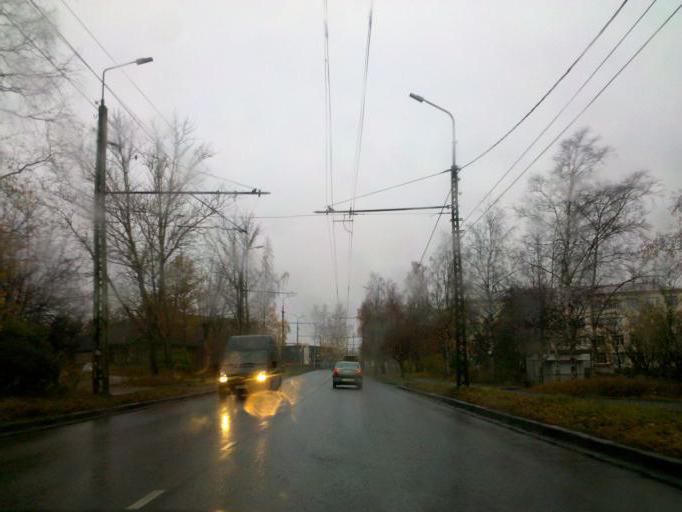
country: RU
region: Republic of Karelia
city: Petrozavodsk
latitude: 61.8000
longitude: 34.3211
